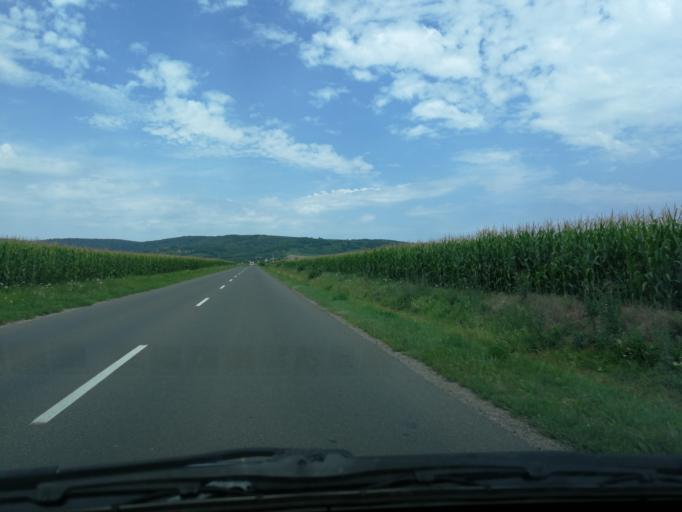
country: HU
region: Baranya
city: Siklos
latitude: 45.8546
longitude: 18.3178
